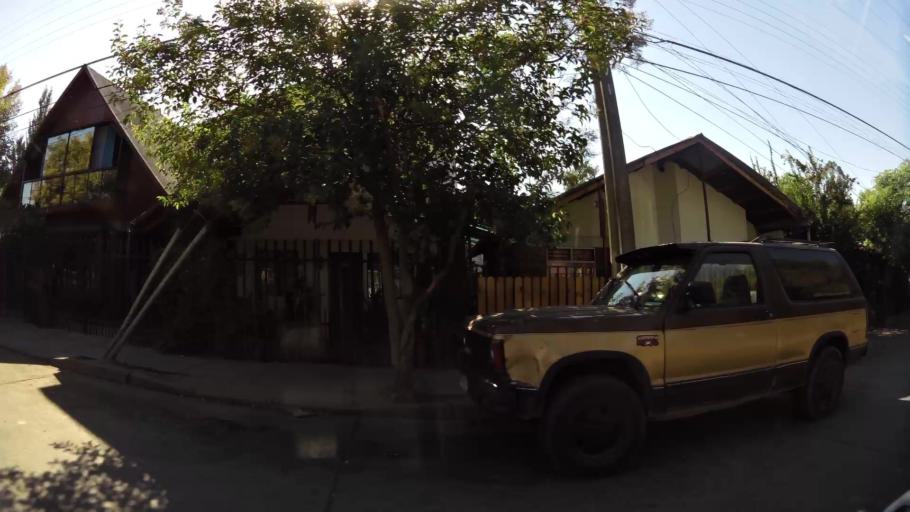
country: CL
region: Maule
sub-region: Provincia de Curico
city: Curico
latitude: -34.9993
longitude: -71.2458
